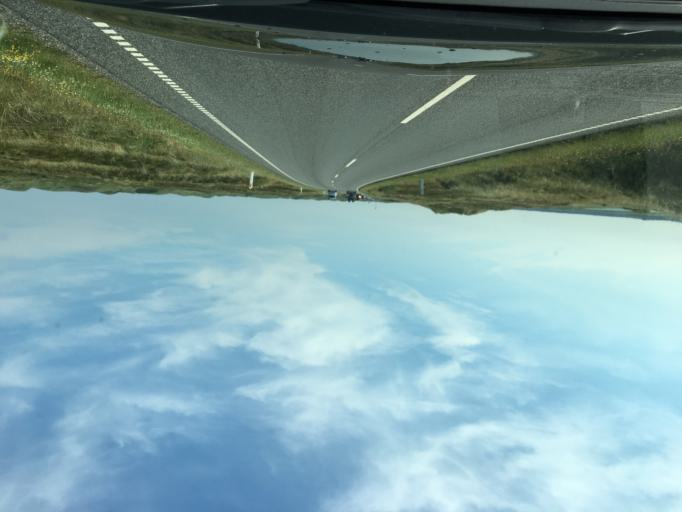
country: DK
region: Central Jutland
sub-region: Ringkobing-Skjern Kommune
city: Hvide Sande
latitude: 55.8424
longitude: 8.1731
